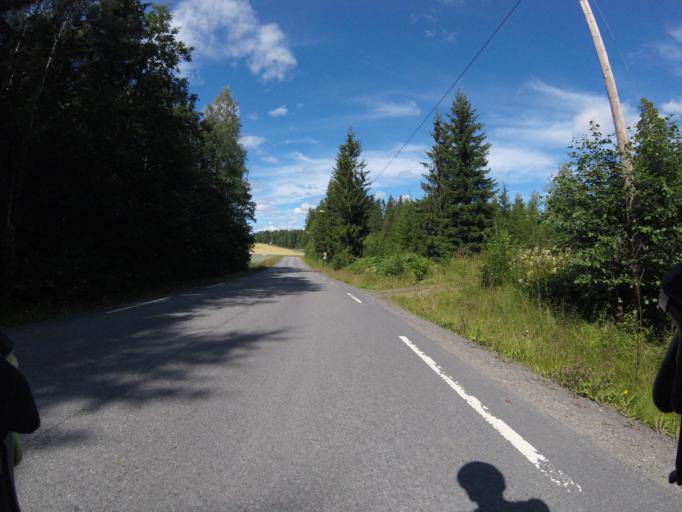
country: NO
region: Akershus
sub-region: Lorenskog
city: Kjenn
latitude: 59.9026
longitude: 10.9673
